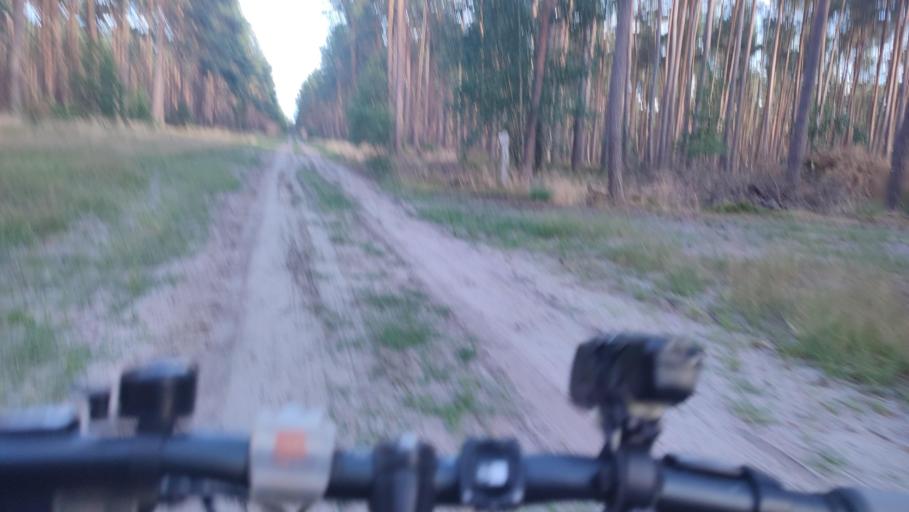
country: DE
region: Lower Saxony
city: Hitzacker
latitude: 53.2280
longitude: 11.0297
